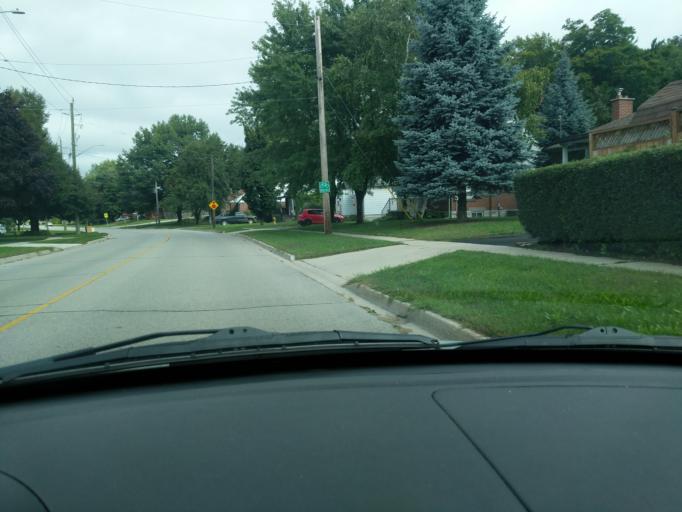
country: CA
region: Ontario
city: Cambridge
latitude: 43.4234
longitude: -80.3158
